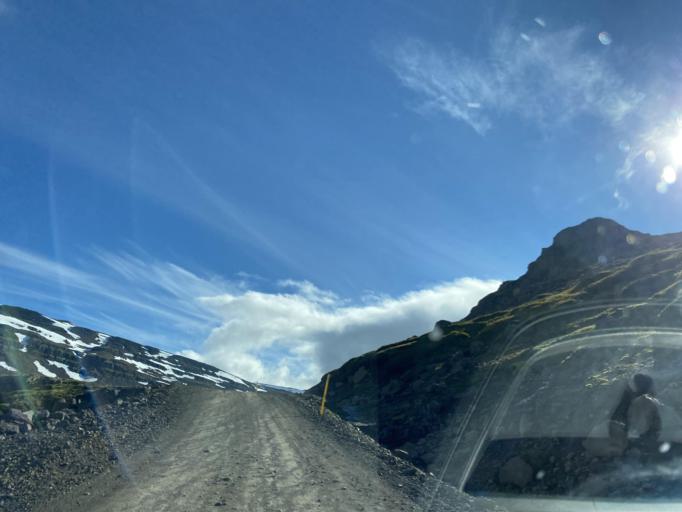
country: IS
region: East
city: Eskifjoerdur
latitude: 65.1758
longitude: -14.1127
